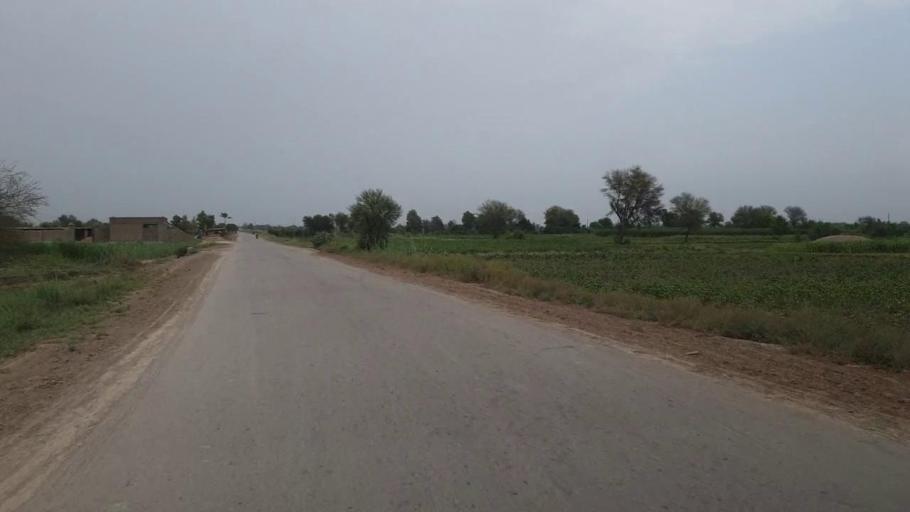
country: PK
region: Sindh
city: Bandhi
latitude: 26.5339
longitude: 68.2193
